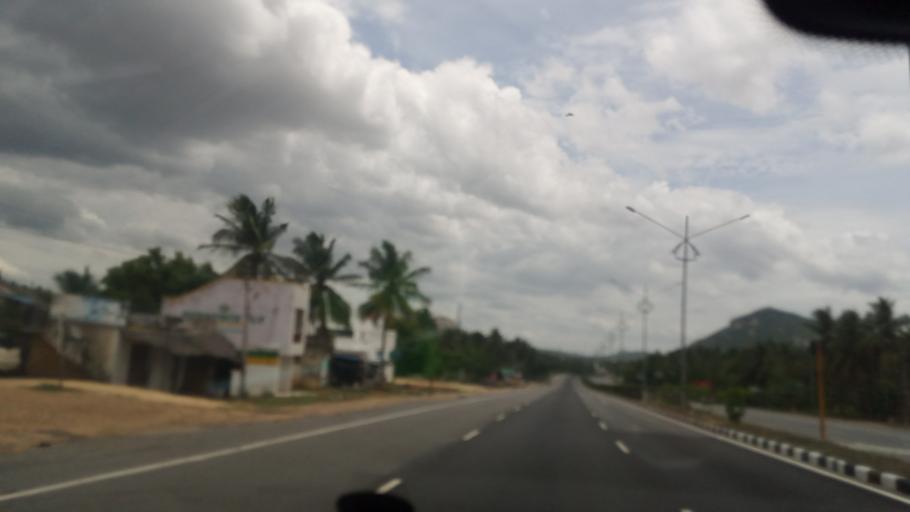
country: IN
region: Tamil Nadu
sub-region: Vellore
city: Jolarpettai
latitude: 12.5716
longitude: 78.4771
